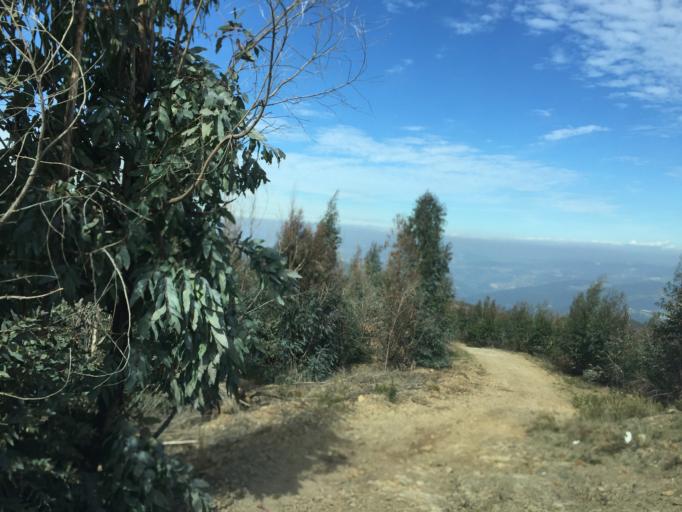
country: PT
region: Aveiro
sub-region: Arouca
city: Arouca
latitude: 40.9643
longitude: -8.2397
